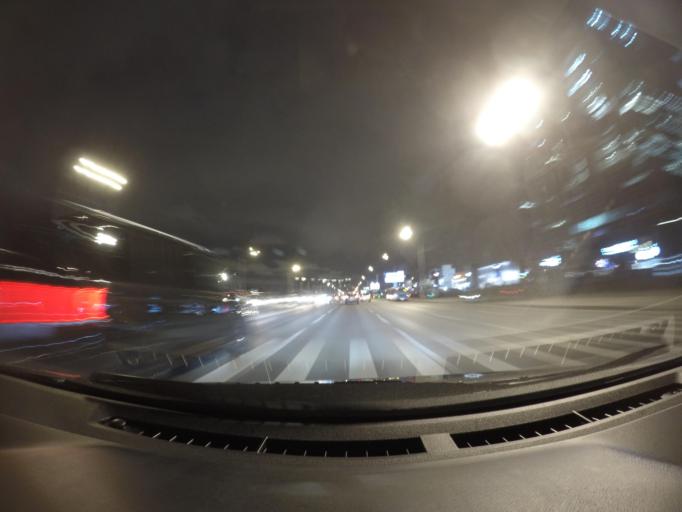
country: RU
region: Moscow
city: Tekstil'shchiki
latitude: 55.7132
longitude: 37.7188
